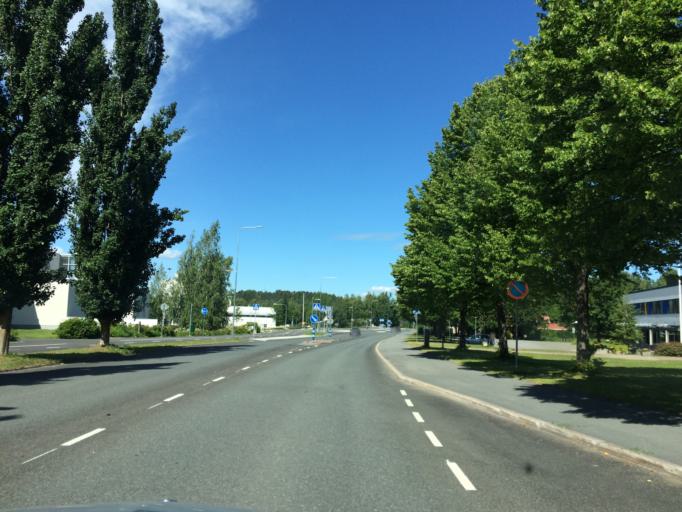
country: FI
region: Haeme
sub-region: Haemeenlinna
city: Haemeenlinna
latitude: 60.9858
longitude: 24.4413
